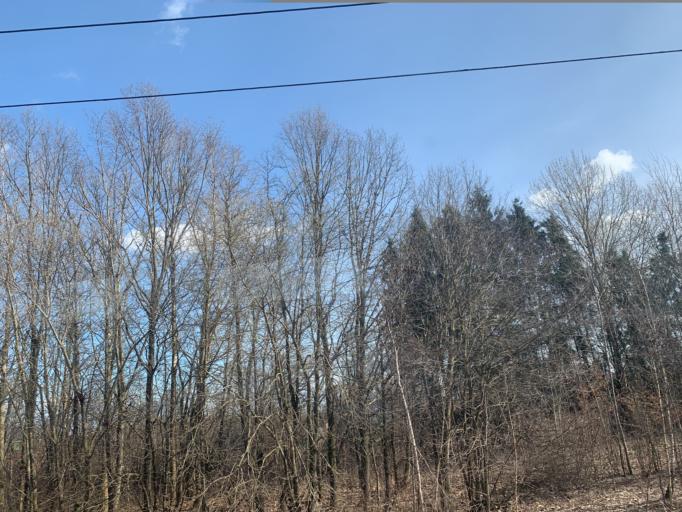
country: BY
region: Minsk
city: Stan'kava
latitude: 53.6923
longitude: 27.2353
